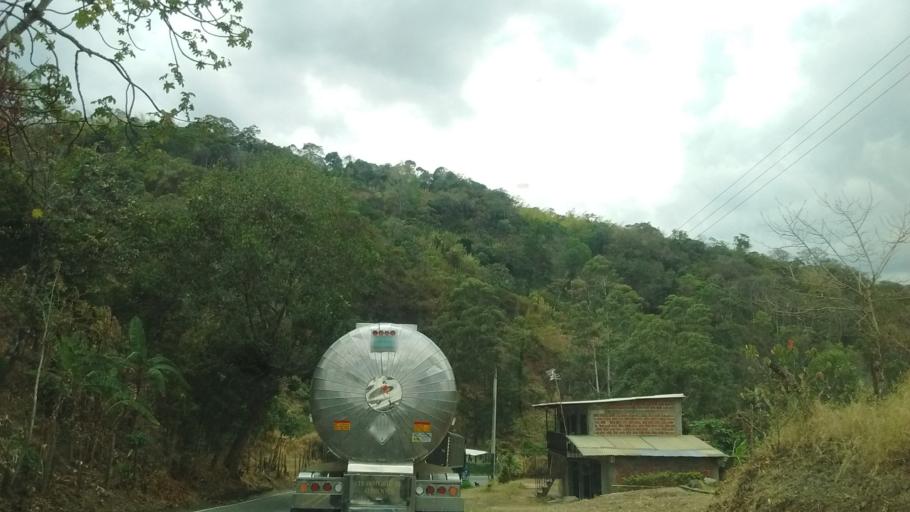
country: CO
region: Cauca
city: Rosas
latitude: 2.2954
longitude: -76.7074
